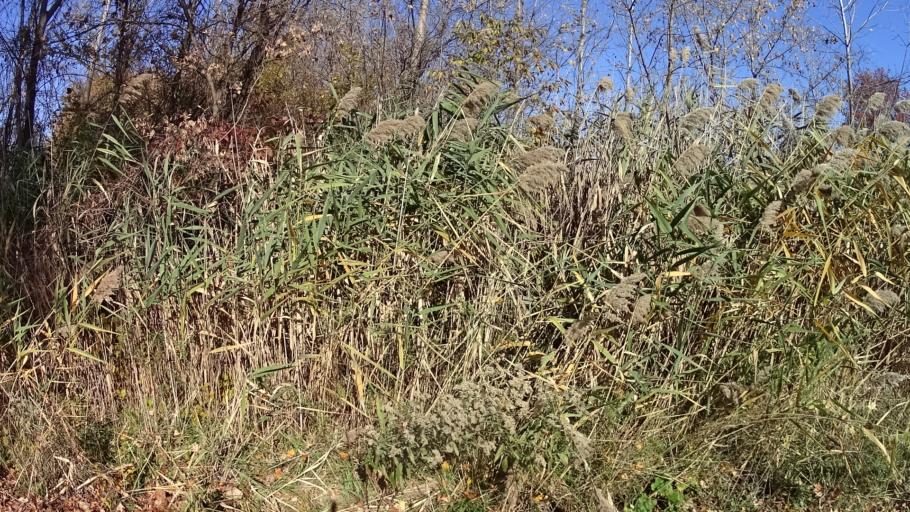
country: US
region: Ohio
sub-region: Lorain County
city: Lorain
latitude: 41.4644
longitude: -82.1617
